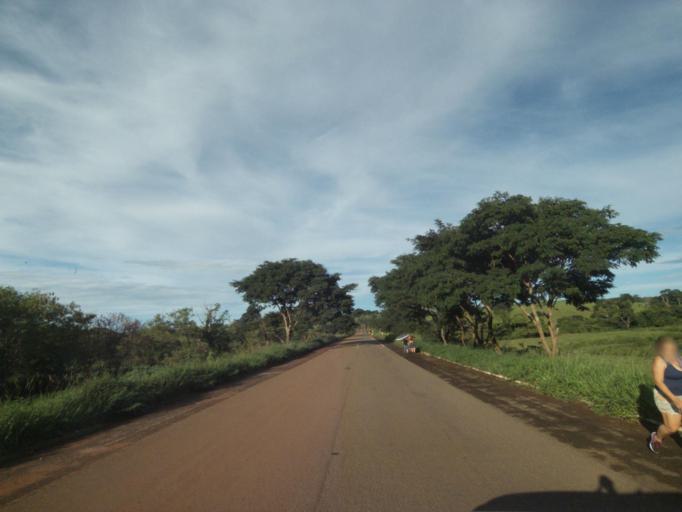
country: BR
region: Goias
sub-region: Itaberai
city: Itaberai
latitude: -15.9170
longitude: -49.5942
